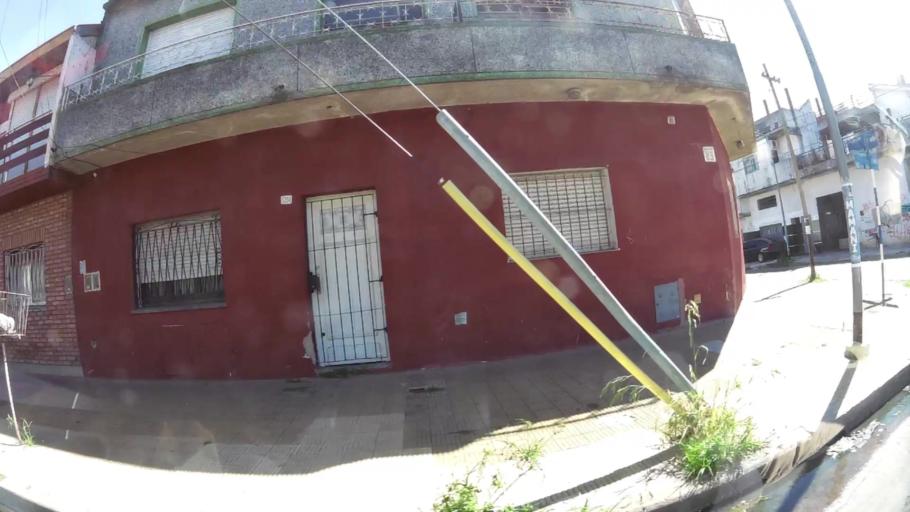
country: AR
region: Buenos Aires
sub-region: Partido de General San Martin
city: General San Martin
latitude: -34.5537
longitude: -58.5673
